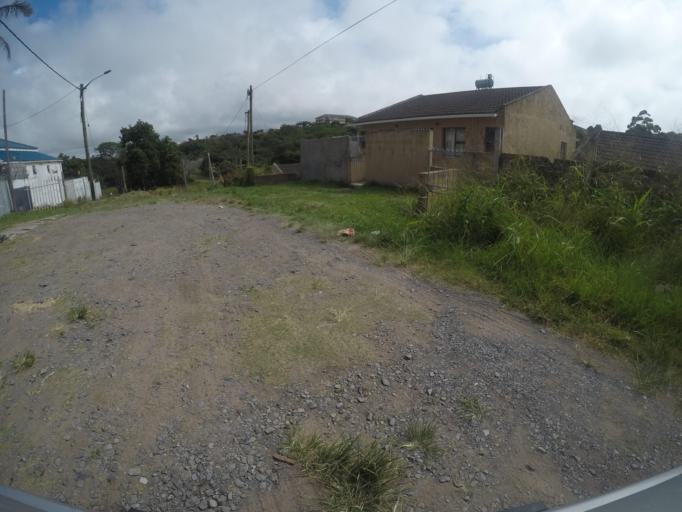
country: ZA
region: Eastern Cape
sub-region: Buffalo City Metropolitan Municipality
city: East London
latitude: -32.9988
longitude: 27.9119
